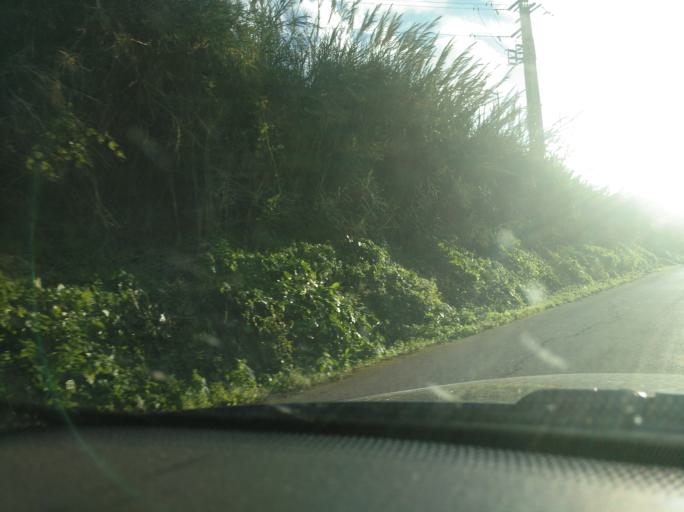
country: PT
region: Lisbon
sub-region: Loures
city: Unhos
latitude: 38.8346
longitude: -9.1314
